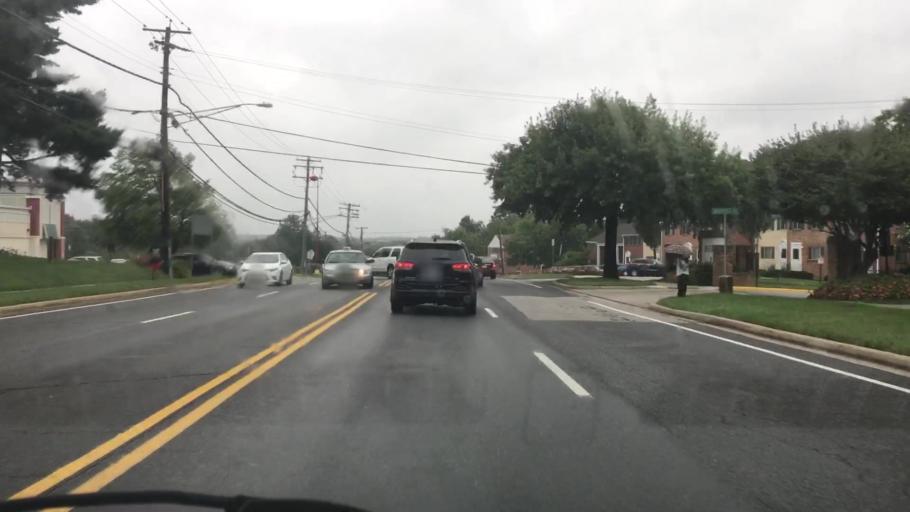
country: US
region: Maryland
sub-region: Prince George's County
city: South Laurel
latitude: 39.0735
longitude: -76.8510
